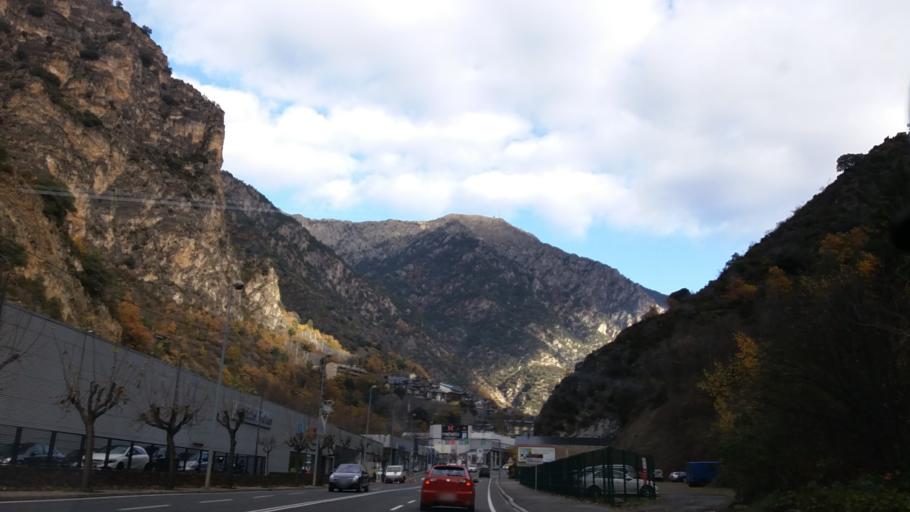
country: AD
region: Sant Julia de Loria
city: Sant Julia de Loria
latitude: 42.4800
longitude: 1.4894
